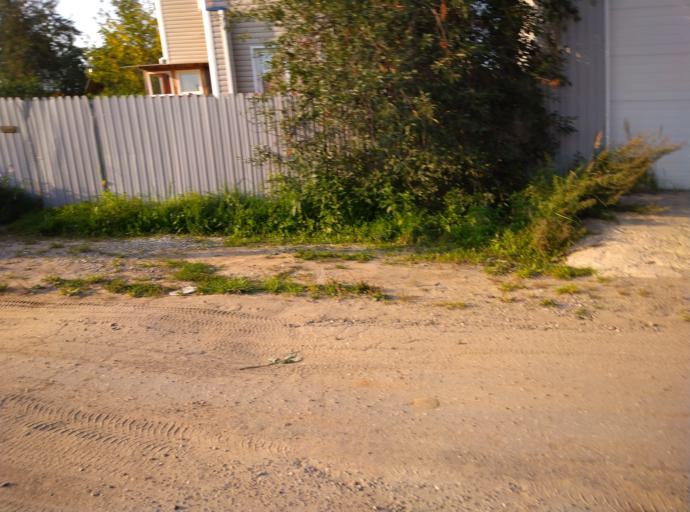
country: RU
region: Kostroma
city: Oktyabr'skiy
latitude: 57.7507
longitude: 40.9679
